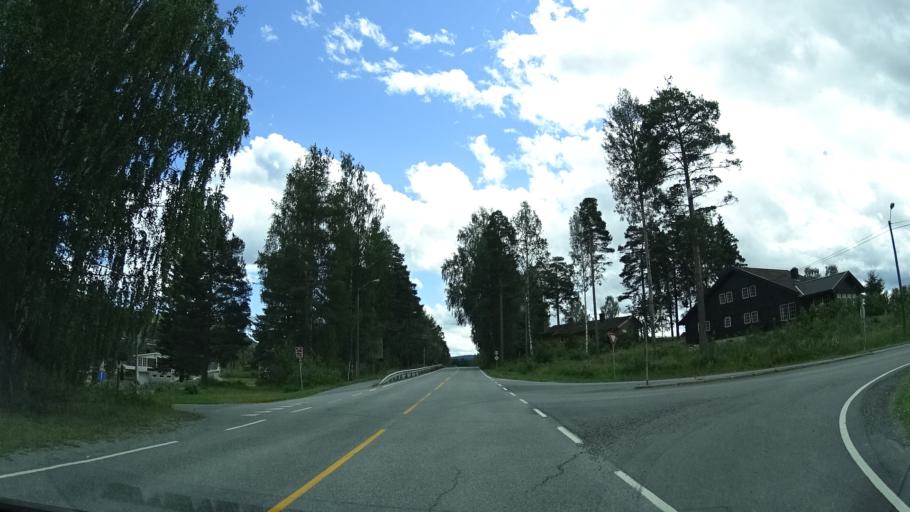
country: NO
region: Buskerud
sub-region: Krodsherad
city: Noresund
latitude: 60.1851
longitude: 9.6144
